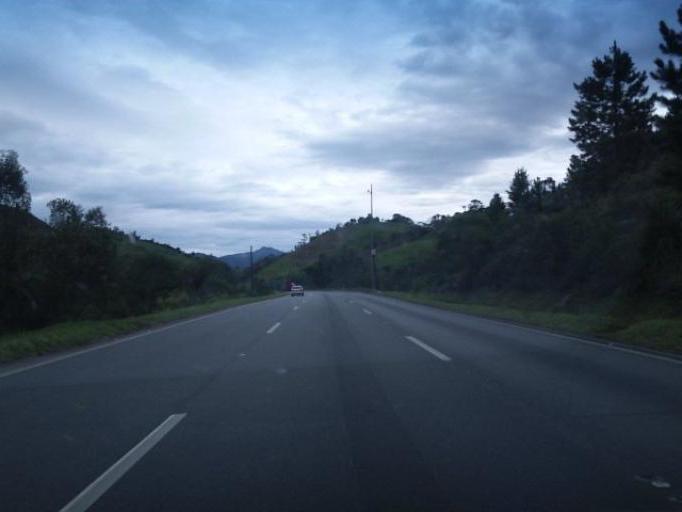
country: BR
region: Sao Paulo
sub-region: Cajati
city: Cajati
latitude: -24.9844
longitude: -48.5072
